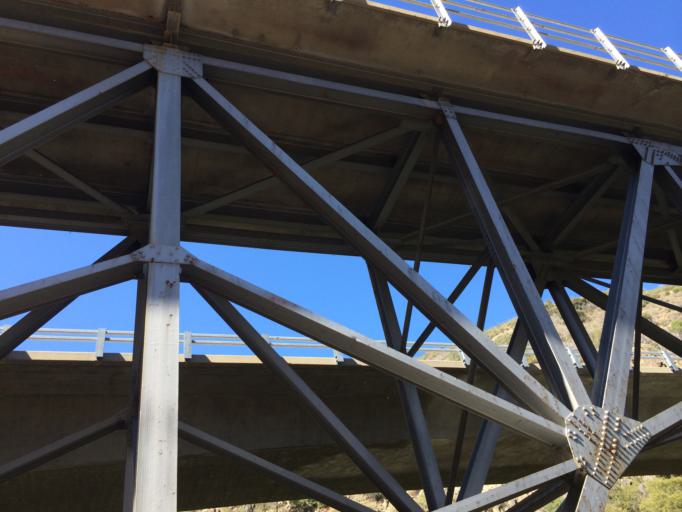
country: US
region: California
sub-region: Kern County
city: Kernville
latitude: 35.9684
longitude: -118.4863
